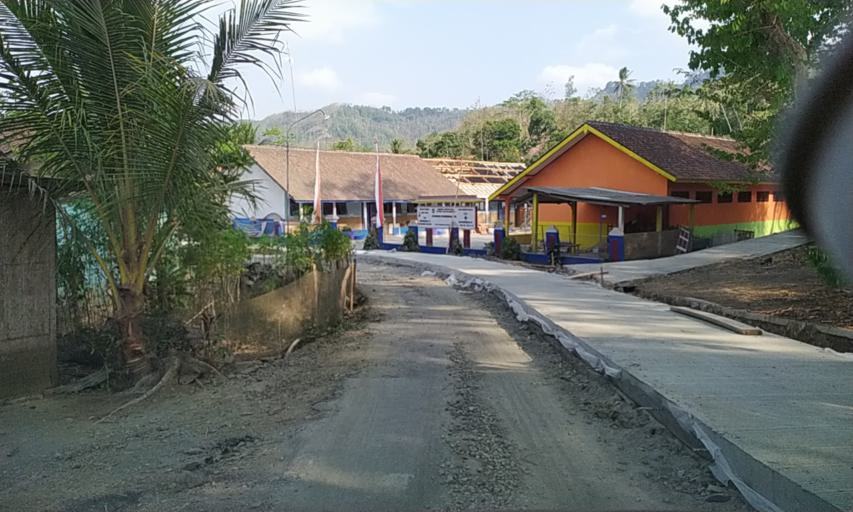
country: ID
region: Central Java
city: Karanggintung
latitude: -7.4849
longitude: 108.9234
